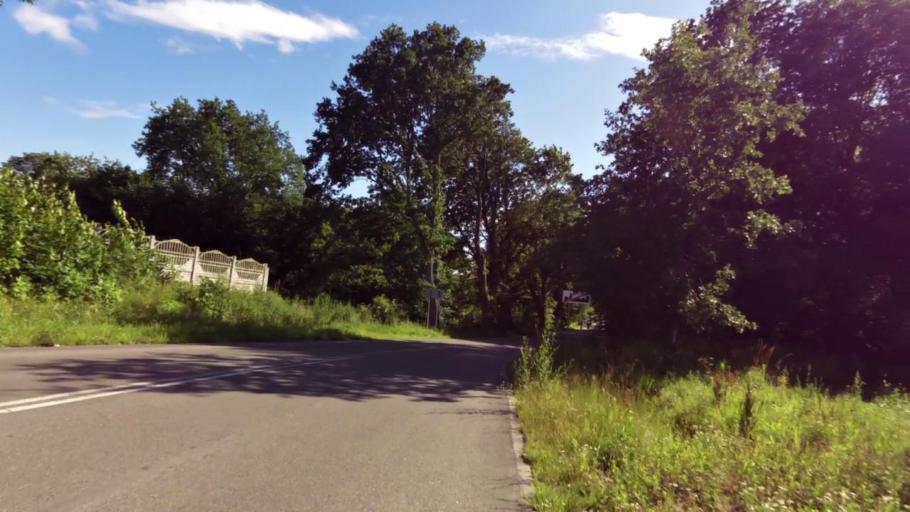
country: PL
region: West Pomeranian Voivodeship
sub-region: Powiat slawienski
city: Slawno
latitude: 54.4545
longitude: 16.7409
